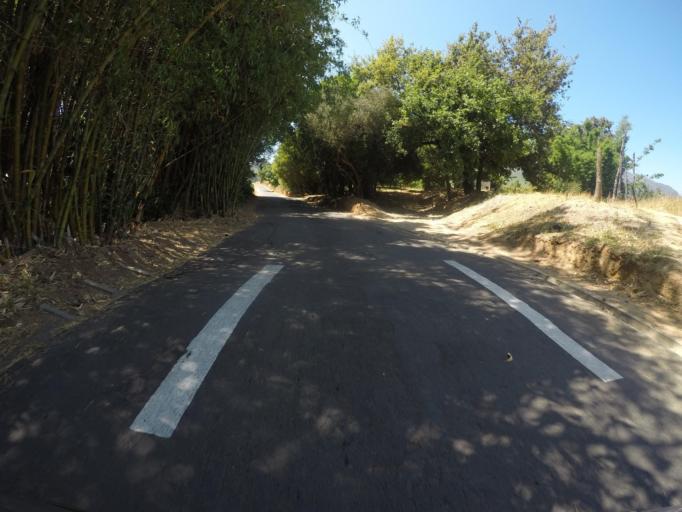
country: ZA
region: Western Cape
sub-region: Cape Winelands District Municipality
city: Stellenbosch
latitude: -33.9957
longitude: 18.8780
